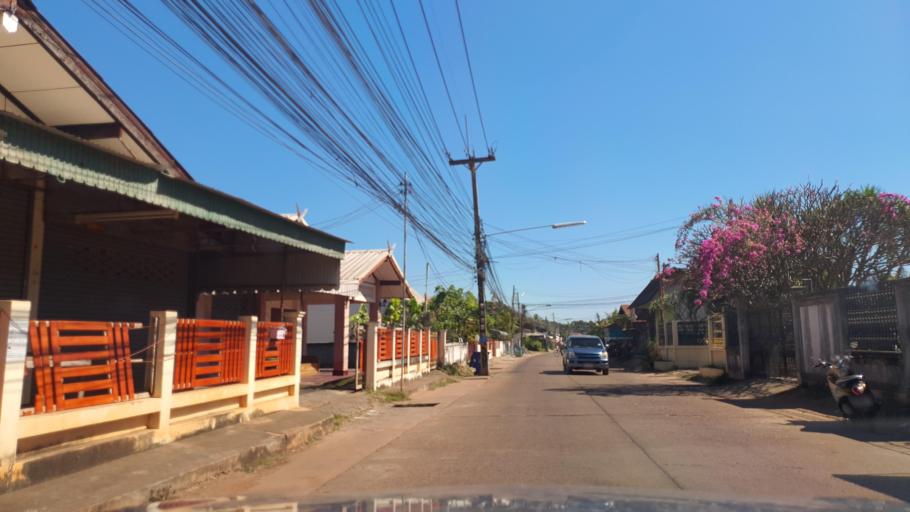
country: TH
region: Sakon Nakhon
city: Sakon Nakhon
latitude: 17.1570
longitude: 104.1216
